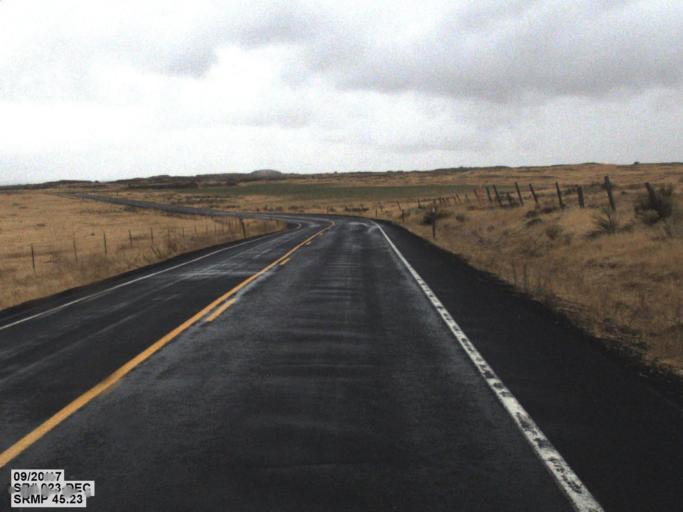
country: US
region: Washington
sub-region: Lincoln County
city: Davenport
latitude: 47.3280
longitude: -117.9833
